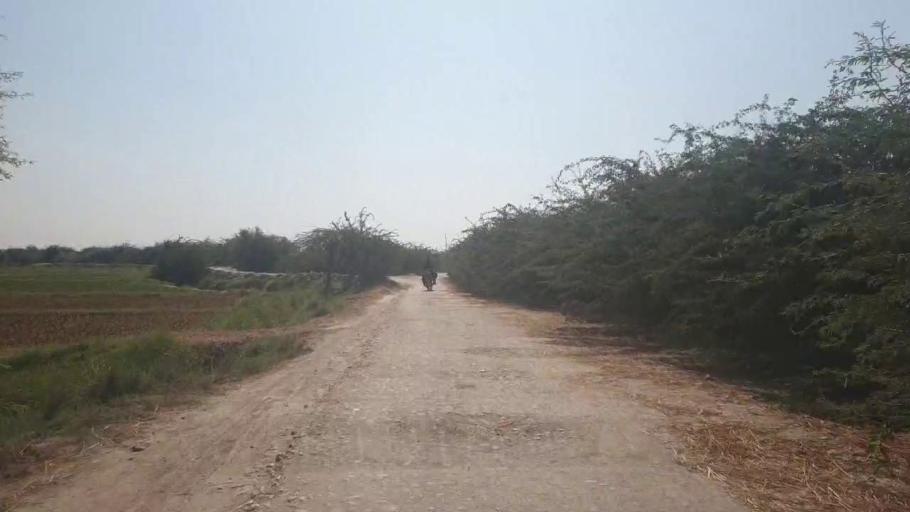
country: PK
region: Sindh
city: Badin
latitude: 24.6561
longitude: 68.9196
